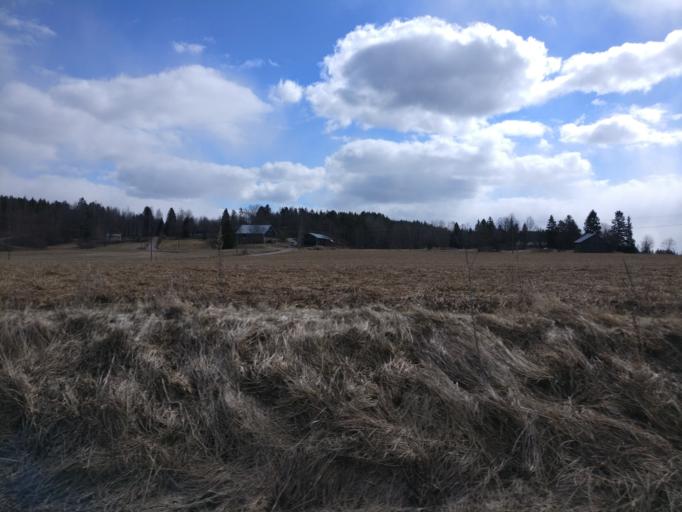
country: FI
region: Uusimaa
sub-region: Helsinki
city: Karjalohja
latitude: 60.2109
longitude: 23.7353
